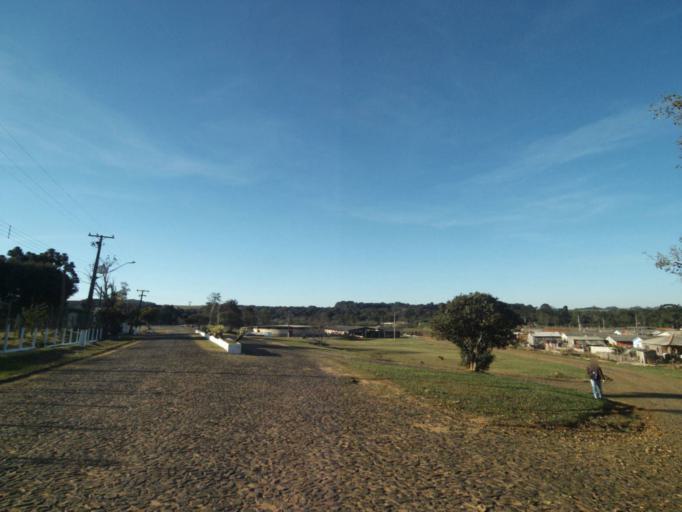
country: BR
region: Parana
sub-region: Tibagi
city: Tibagi
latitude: -24.5049
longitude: -50.4172
